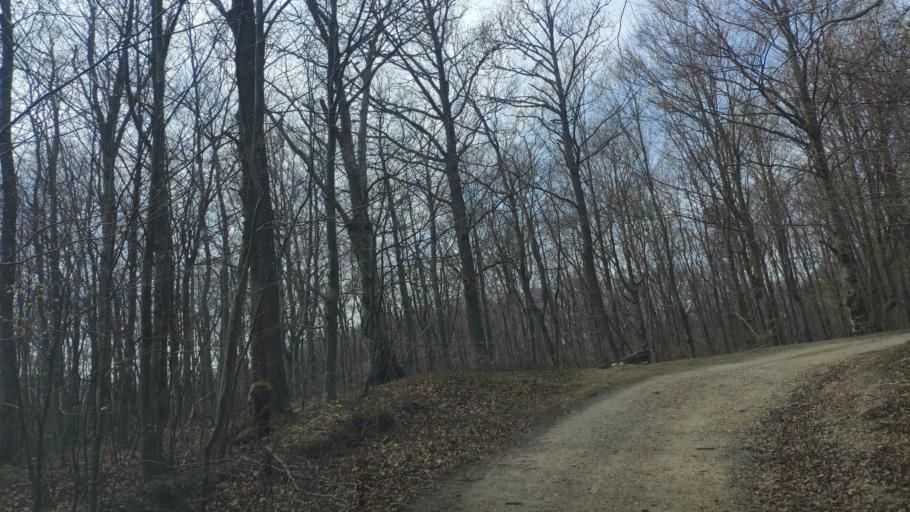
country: SK
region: Kosicky
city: Moldava nad Bodvou
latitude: 48.7476
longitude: 21.0249
